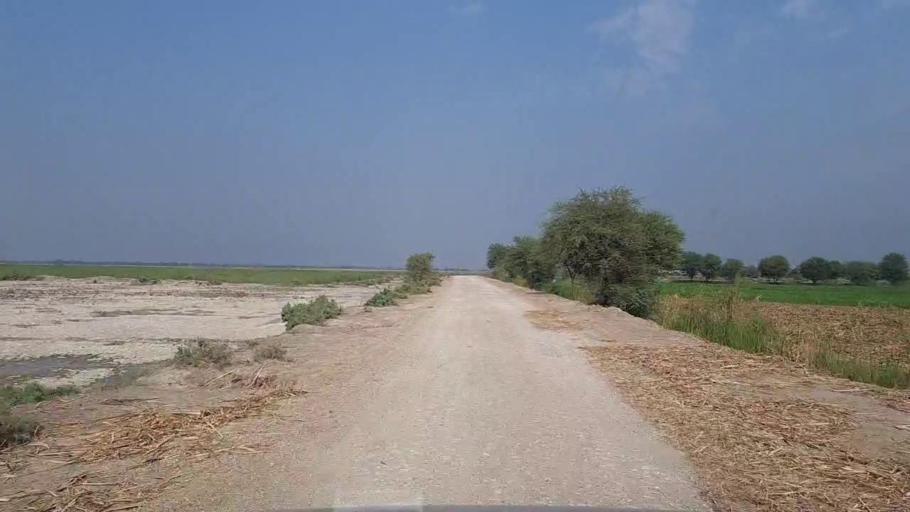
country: PK
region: Sindh
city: Mirwah Gorchani
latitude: 25.3755
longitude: 69.0402
